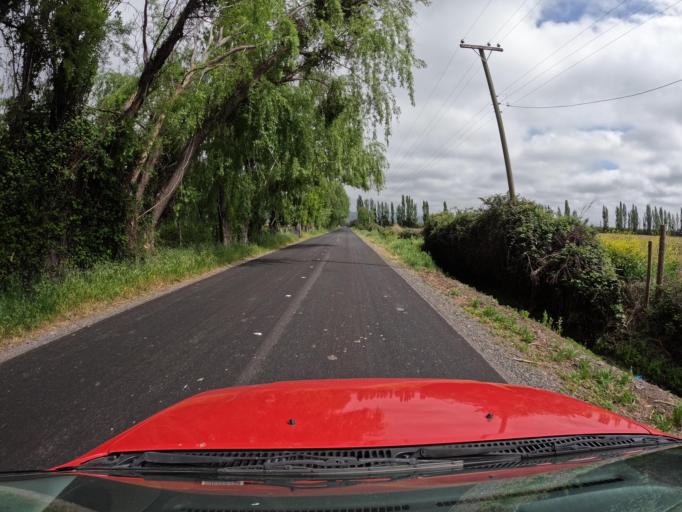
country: CL
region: O'Higgins
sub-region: Provincia de Colchagua
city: Santa Cruz
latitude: -34.6703
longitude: -71.3837
